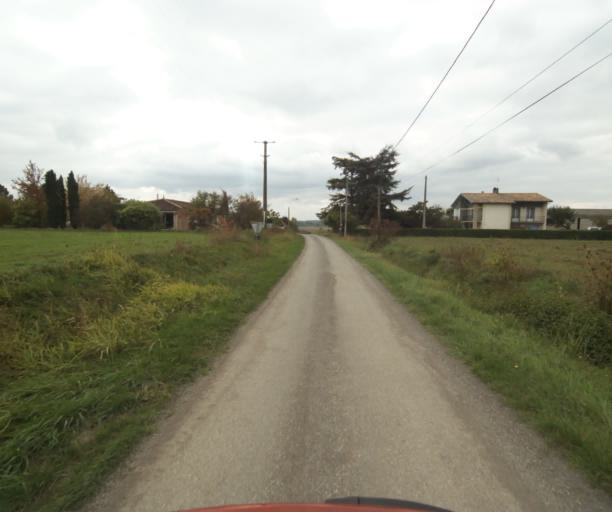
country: FR
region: Midi-Pyrenees
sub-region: Departement du Tarn-et-Garonne
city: Finhan
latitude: 43.8962
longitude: 1.2347
